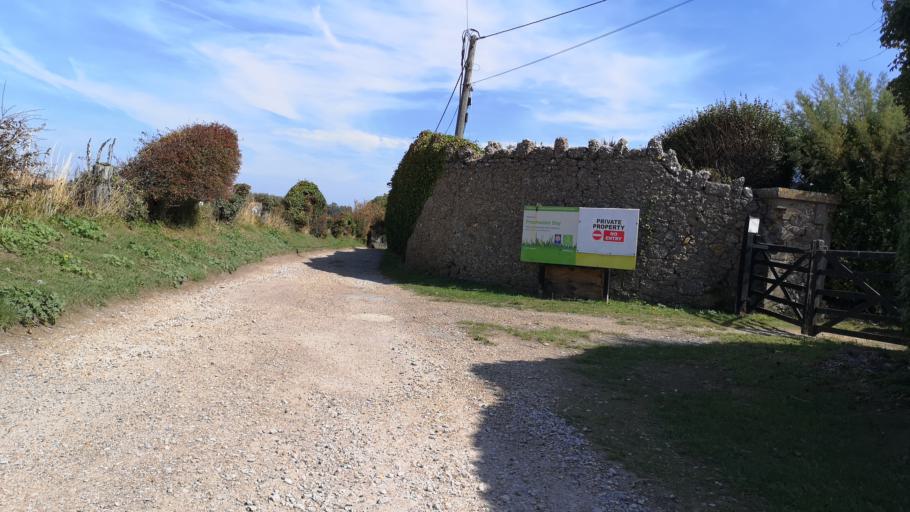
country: GB
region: England
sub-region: Isle of Wight
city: Freshwater
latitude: 50.6696
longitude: -1.5145
